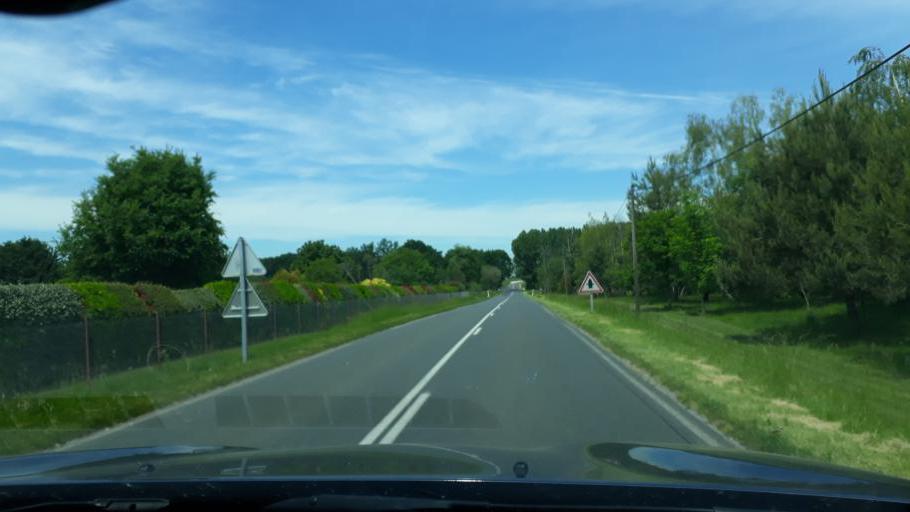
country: FR
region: Centre
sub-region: Departement du Loiret
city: Boynes
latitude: 48.0669
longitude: 2.2860
